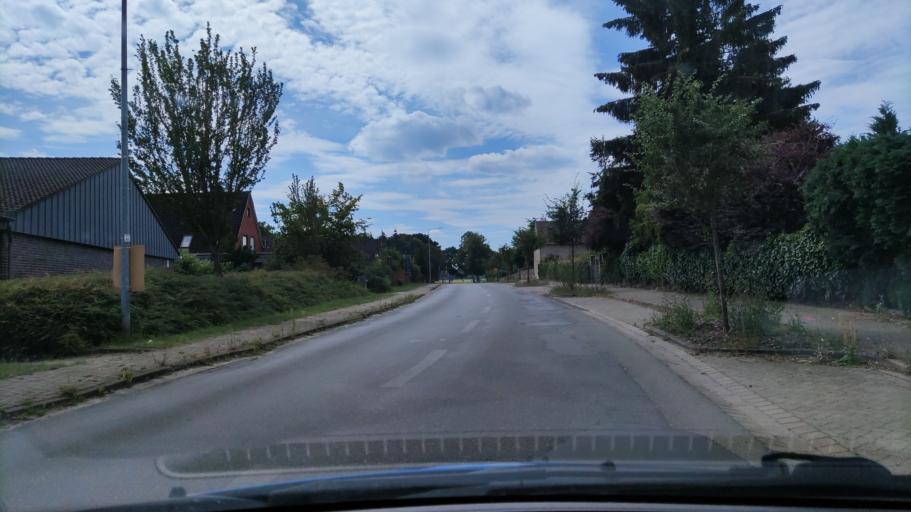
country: DE
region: Lower Saxony
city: Clenze
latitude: 52.9302
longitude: 10.9512
